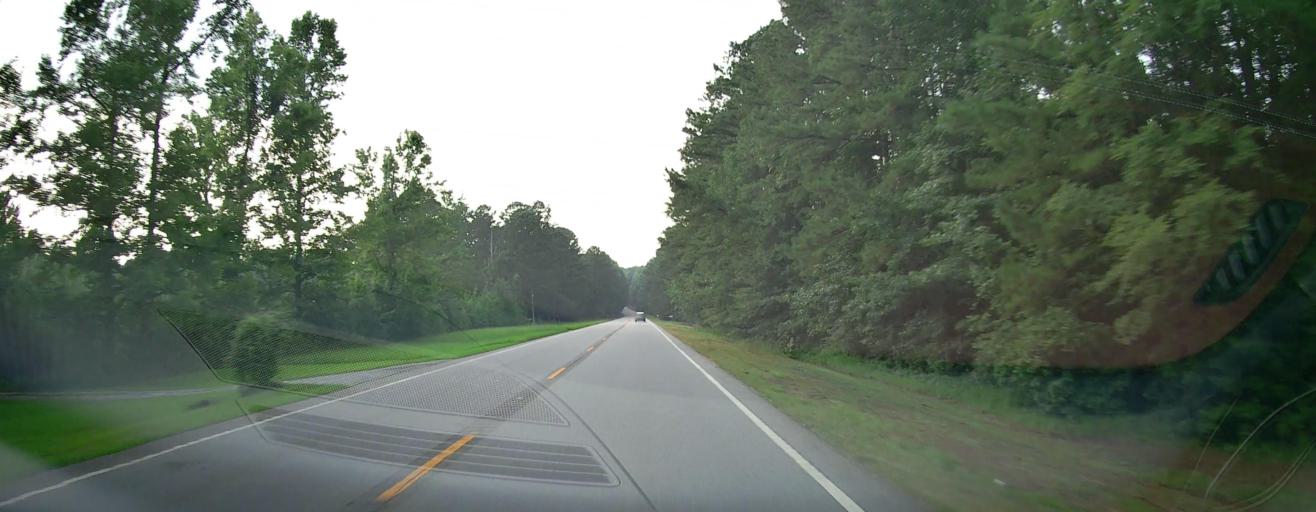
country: US
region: Georgia
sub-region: Monroe County
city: Forsyth
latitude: 33.0600
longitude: -83.7697
